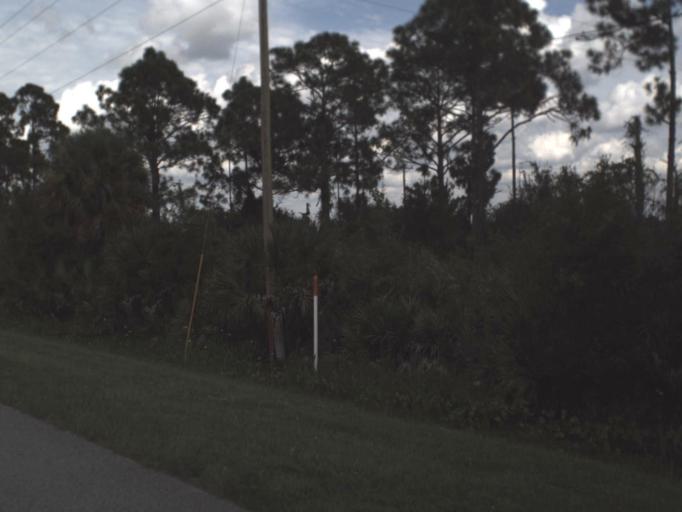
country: US
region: Florida
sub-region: Collier County
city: Immokalee
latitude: 26.5482
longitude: -81.4356
